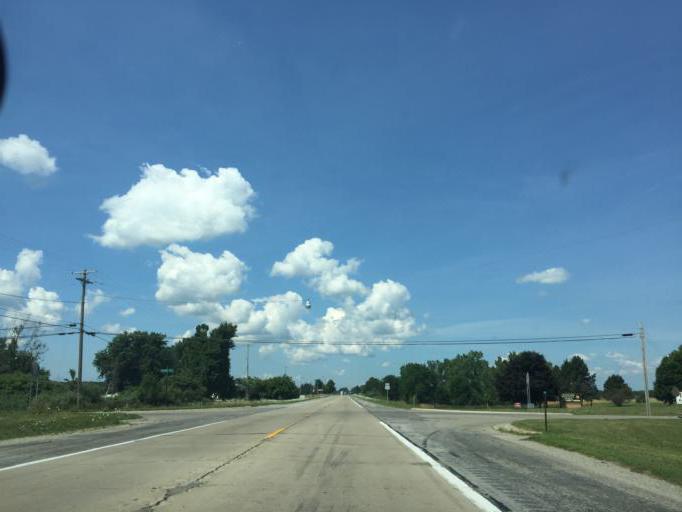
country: US
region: Ohio
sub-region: Lucas County
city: Sylvania
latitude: 41.7974
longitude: -83.7054
